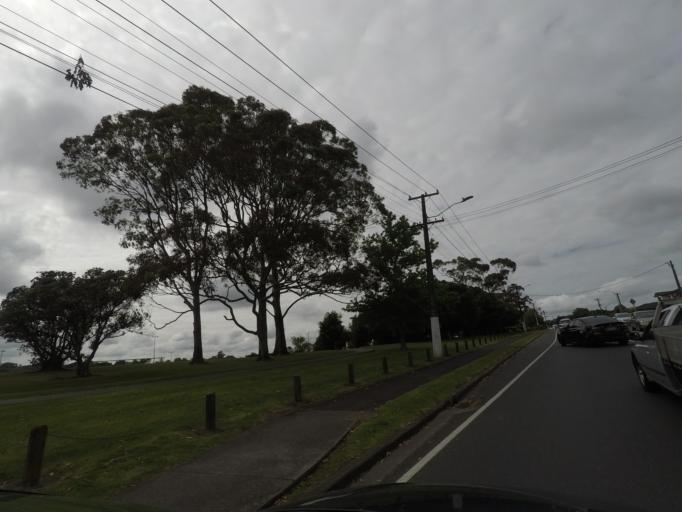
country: NZ
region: Auckland
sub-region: Auckland
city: Waitakere
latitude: -36.9057
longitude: 174.6269
